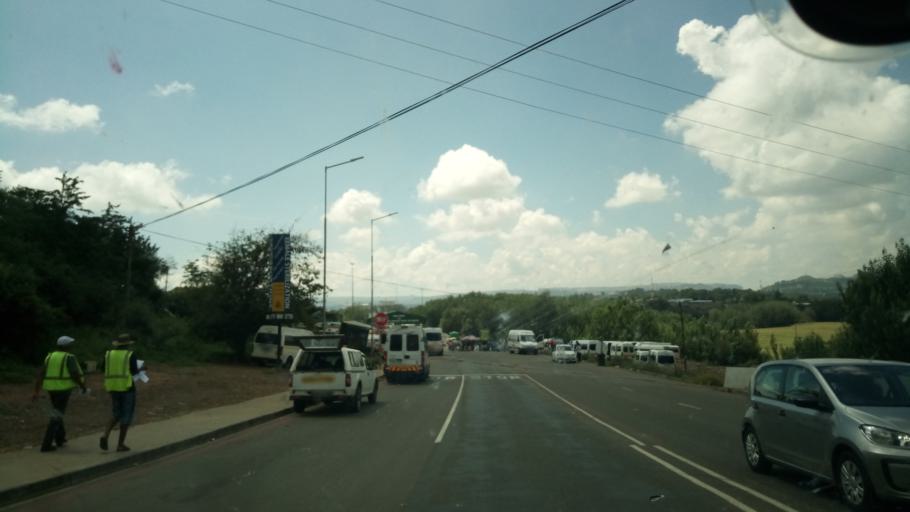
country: LS
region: Maseru
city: Maseru
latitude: -29.2977
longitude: 27.4495
